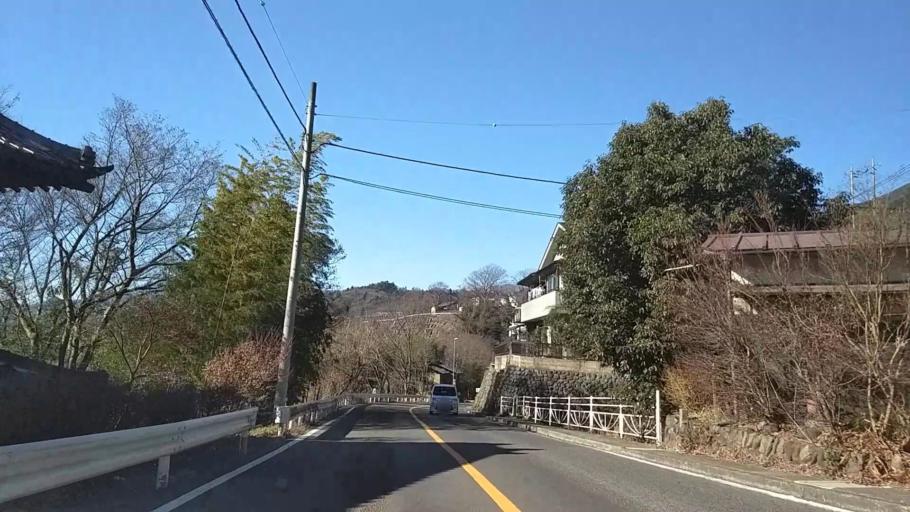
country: JP
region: Yamanashi
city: Otsuki
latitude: 35.6164
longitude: 138.9924
